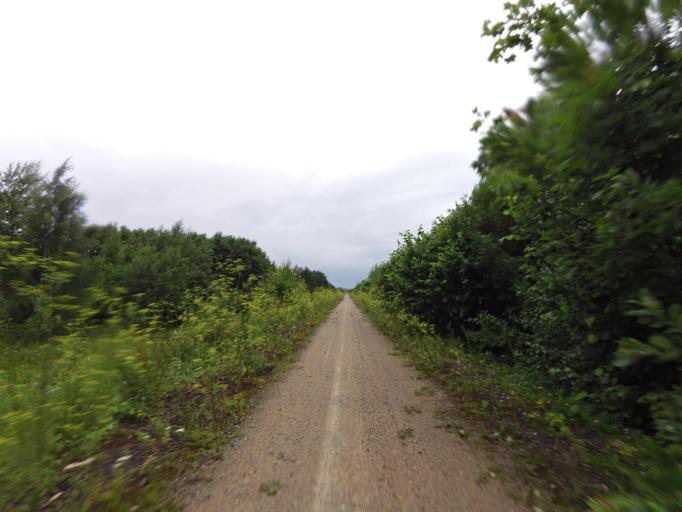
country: EE
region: Laeaene
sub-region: Ridala Parish
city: Uuemoisa
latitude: 58.9523
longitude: 23.7926
